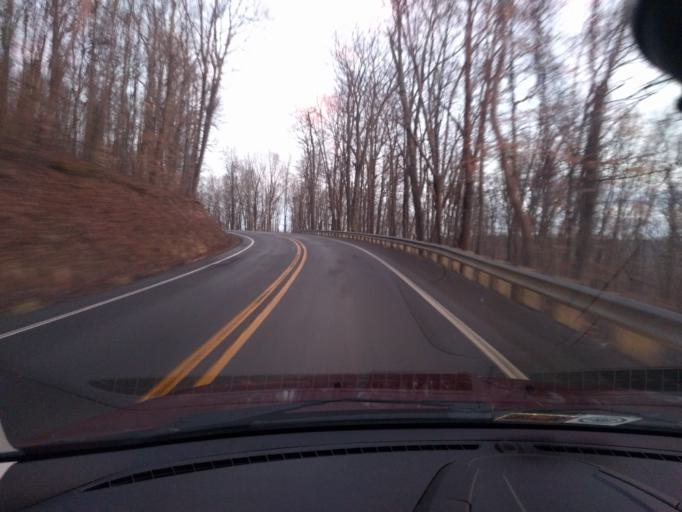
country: US
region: West Virginia
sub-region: Greenbrier County
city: Rainelle
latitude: 37.9908
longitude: -80.8604
